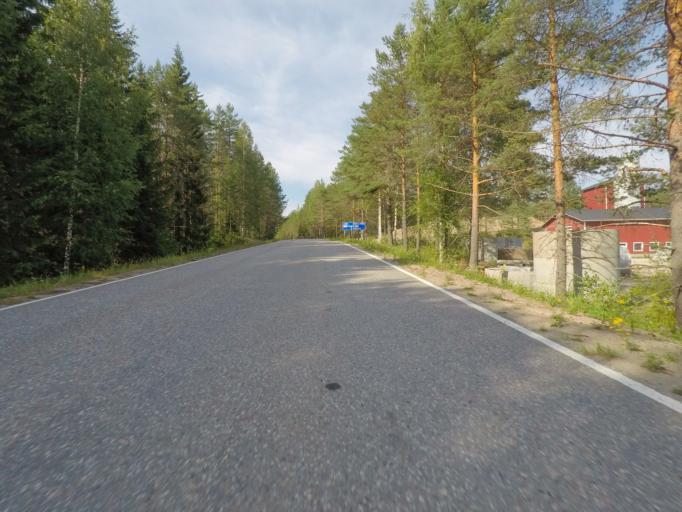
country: FI
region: Southern Savonia
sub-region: Savonlinna
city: Sulkava
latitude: 61.7873
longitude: 28.2432
